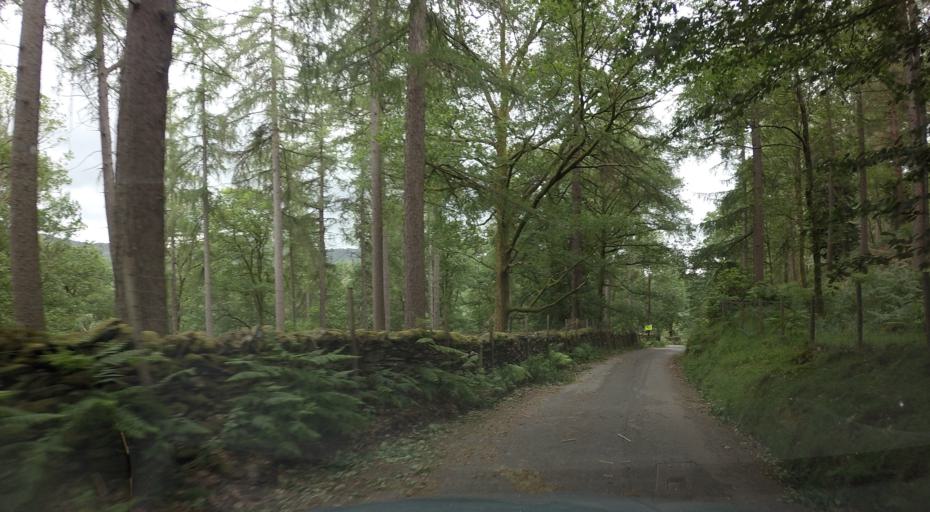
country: GB
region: England
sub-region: Cumbria
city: Keswick
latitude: 54.5605
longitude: -3.1598
